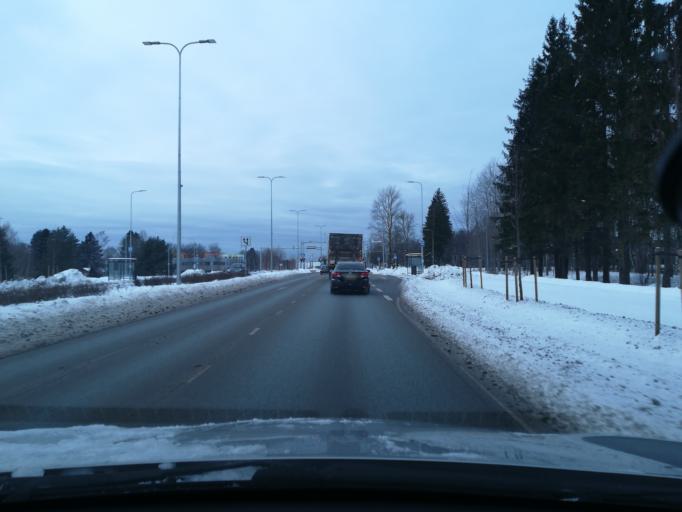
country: EE
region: Harju
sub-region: Saue vald
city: Laagri
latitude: 59.4262
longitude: 24.6333
